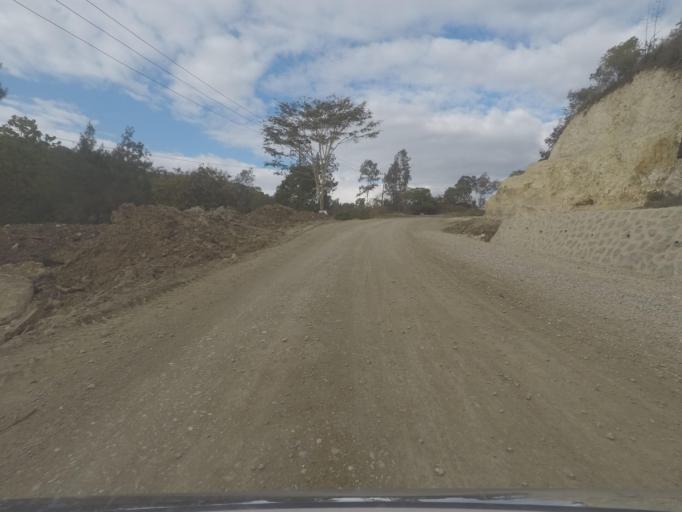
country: TL
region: Baucau
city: Venilale
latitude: -8.6333
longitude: 126.3804
